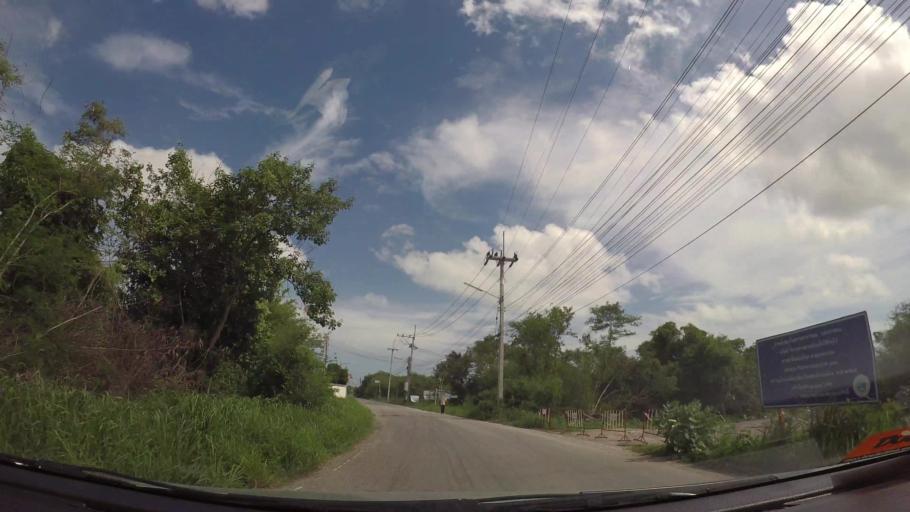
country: TH
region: Chon Buri
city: Sattahip
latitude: 12.6939
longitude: 100.9015
